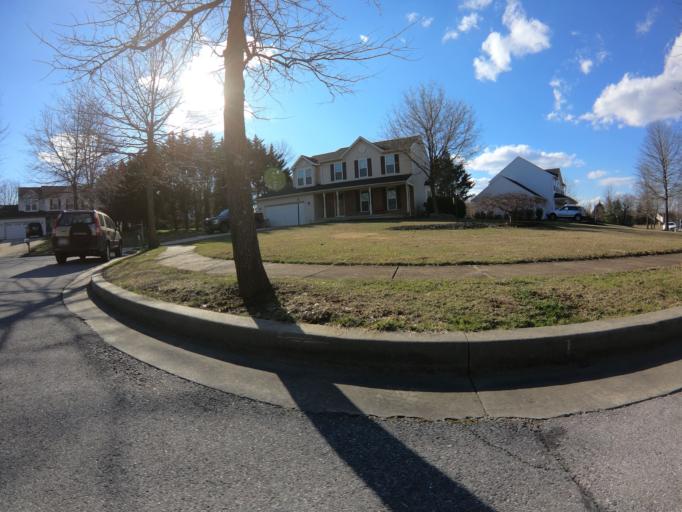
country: US
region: Maryland
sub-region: Howard County
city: Ellicott City
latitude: 39.2519
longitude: -76.8030
